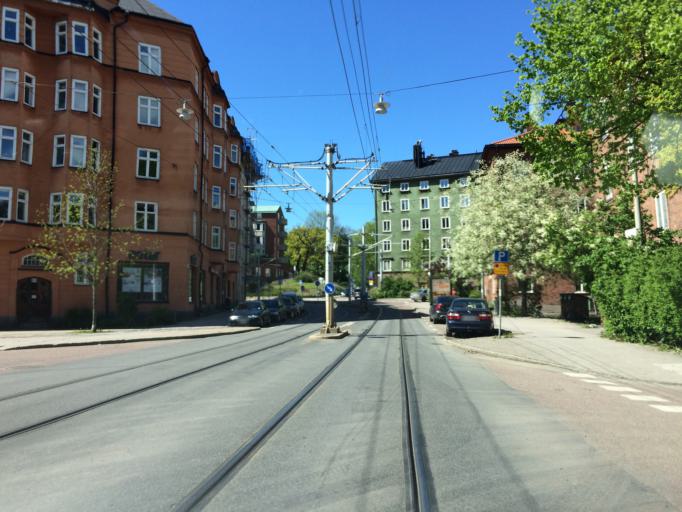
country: SE
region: Stockholm
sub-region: Stockholms Kommun
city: Arsta
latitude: 59.3157
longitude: 18.0144
